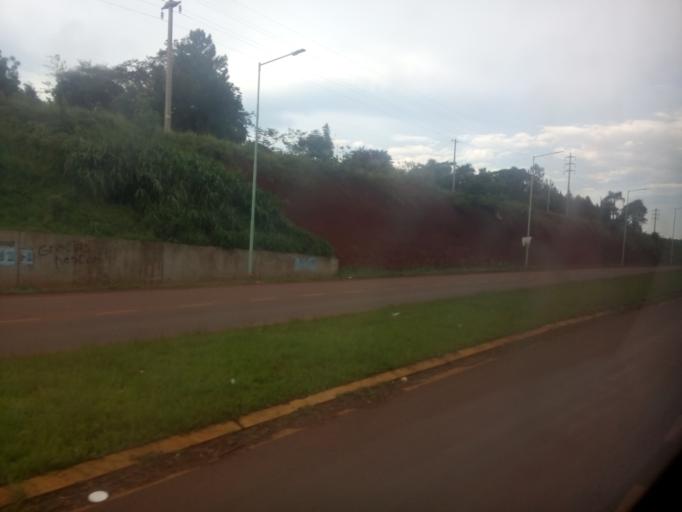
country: AR
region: Misiones
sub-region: Departamento de Obera
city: Obera
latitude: -27.5099
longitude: -55.1373
